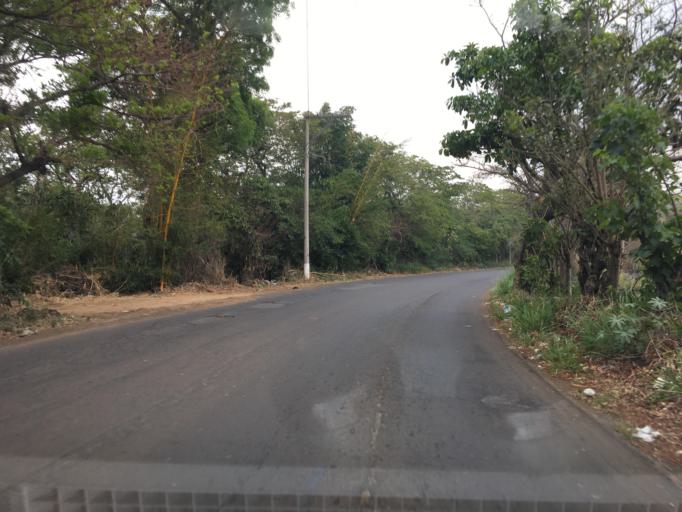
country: GT
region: Guatemala
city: Fraijanes
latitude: 14.3871
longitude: -90.4896
